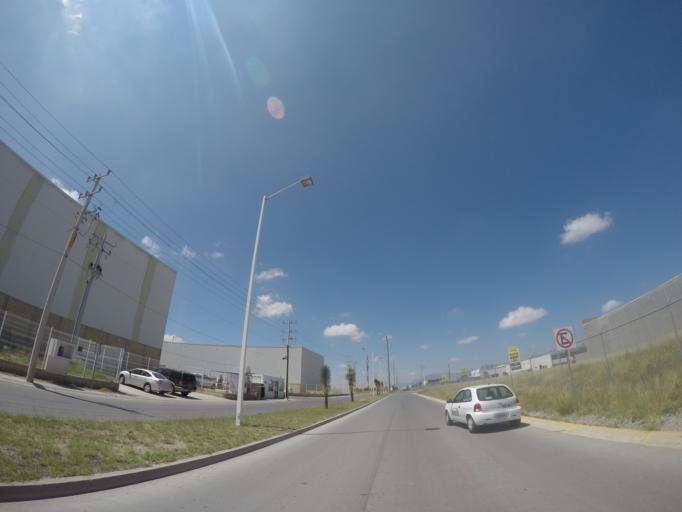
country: MX
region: San Luis Potosi
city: La Pila
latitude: 21.9762
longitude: -100.8728
